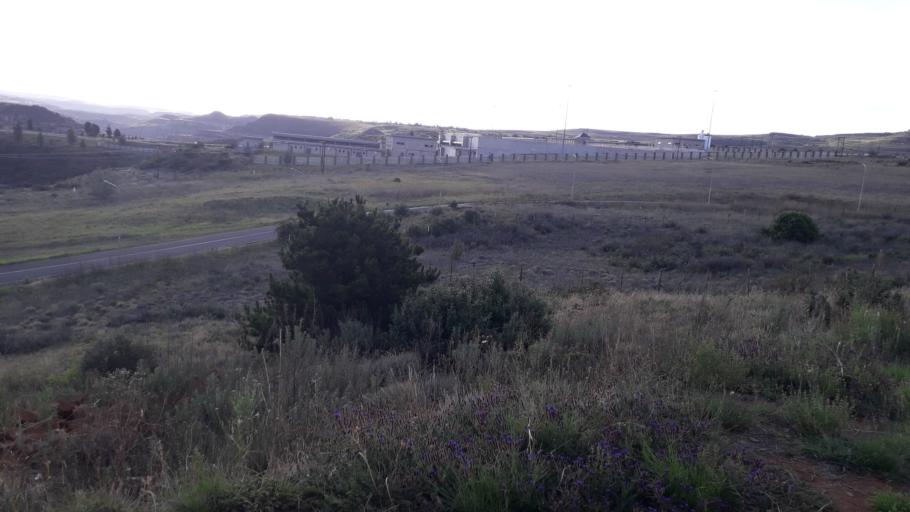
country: LS
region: Berea
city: Teyateyaneng
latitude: -29.3345
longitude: 27.7754
